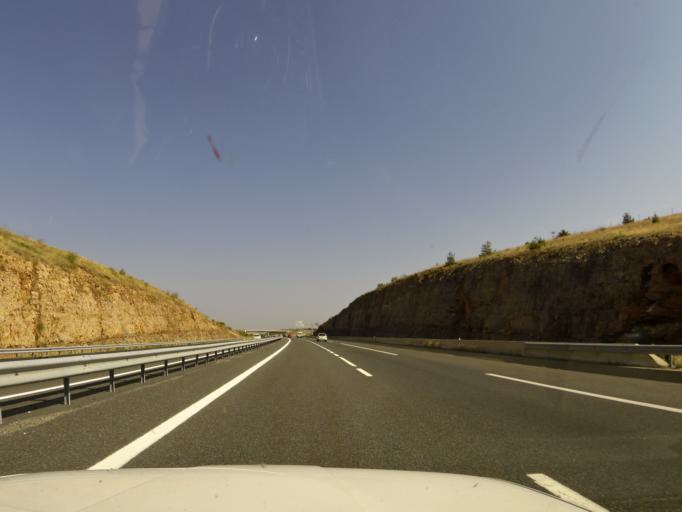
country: FR
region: Midi-Pyrenees
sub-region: Departement de l'Aveyron
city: Creissels
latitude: 44.0378
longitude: 3.0604
